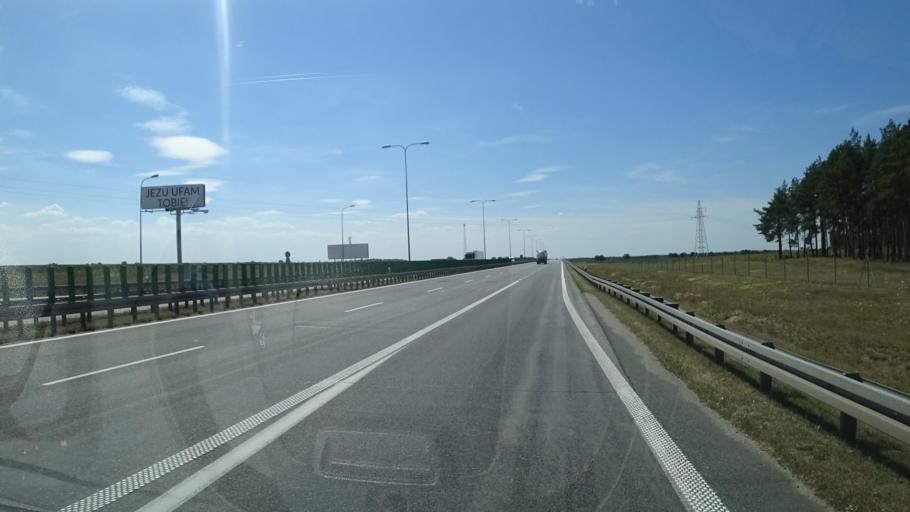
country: PL
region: Lubusz
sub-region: Powiat swiebodzinski
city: Zbaszynek
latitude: 52.3124
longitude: 15.7796
